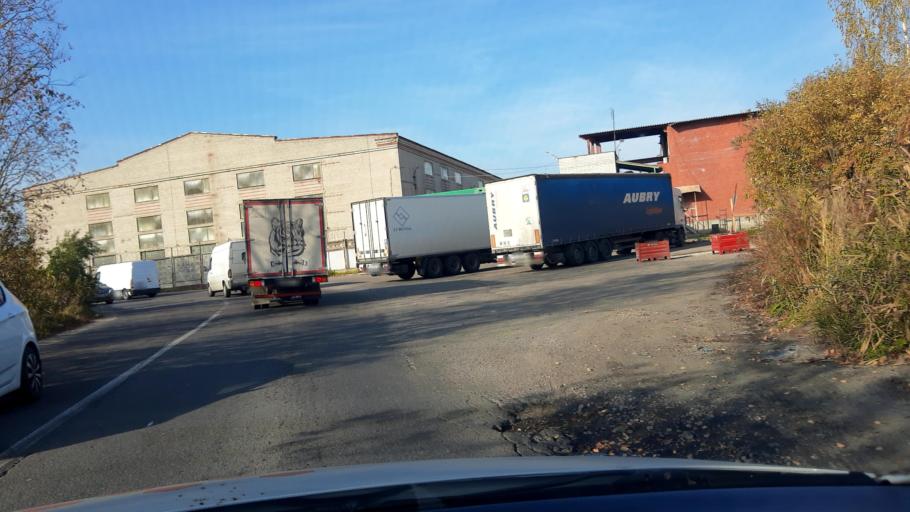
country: RU
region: Moskovskaya
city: Fryazevo
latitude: 55.7671
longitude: 38.4996
